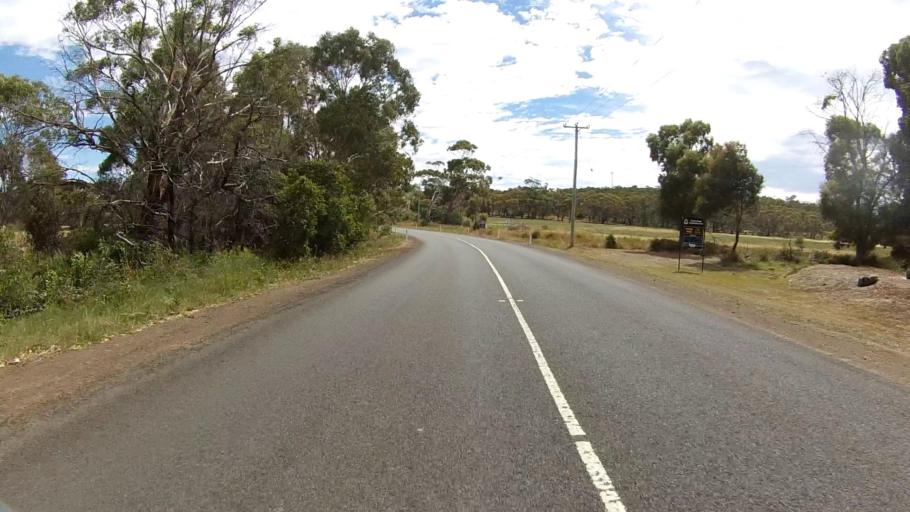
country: AU
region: Tasmania
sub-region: Sorell
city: Sorell
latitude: -42.8857
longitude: 147.6690
